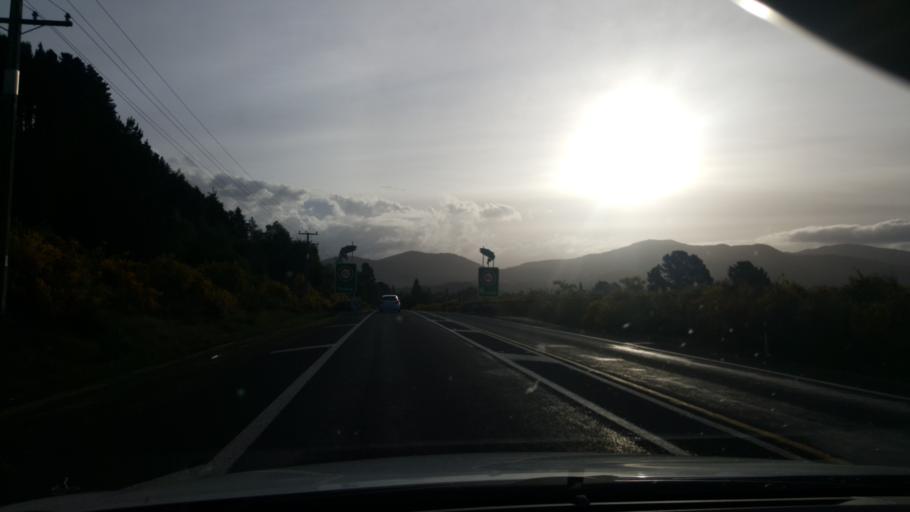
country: NZ
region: Waikato
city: Turangi
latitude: -38.9802
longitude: 175.8255
